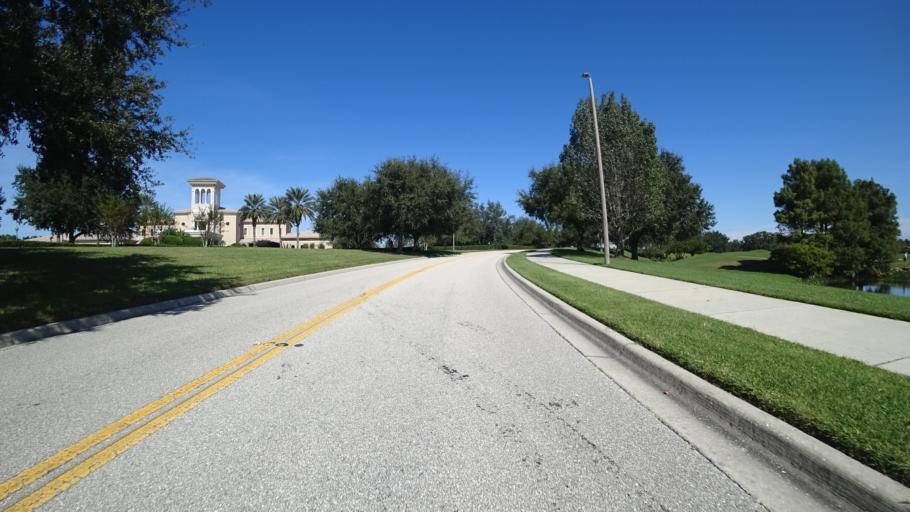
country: US
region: Florida
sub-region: Sarasota County
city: The Meadows
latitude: 27.4029
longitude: -82.4113
